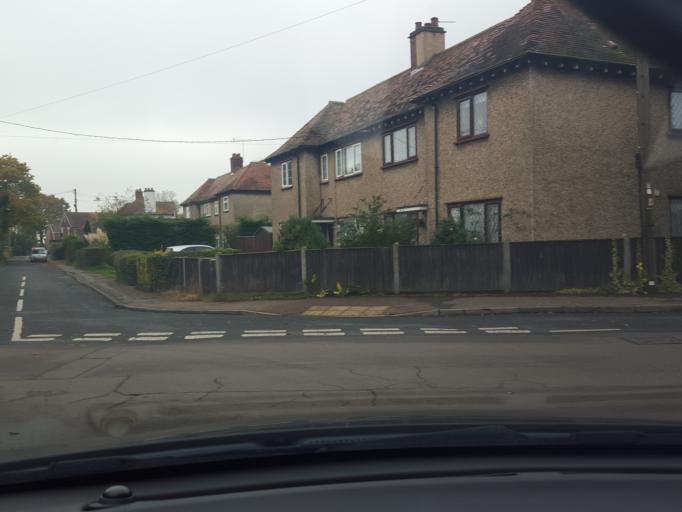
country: GB
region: England
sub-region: Essex
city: Great Bentley
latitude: 51.8412
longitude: 1.0404
